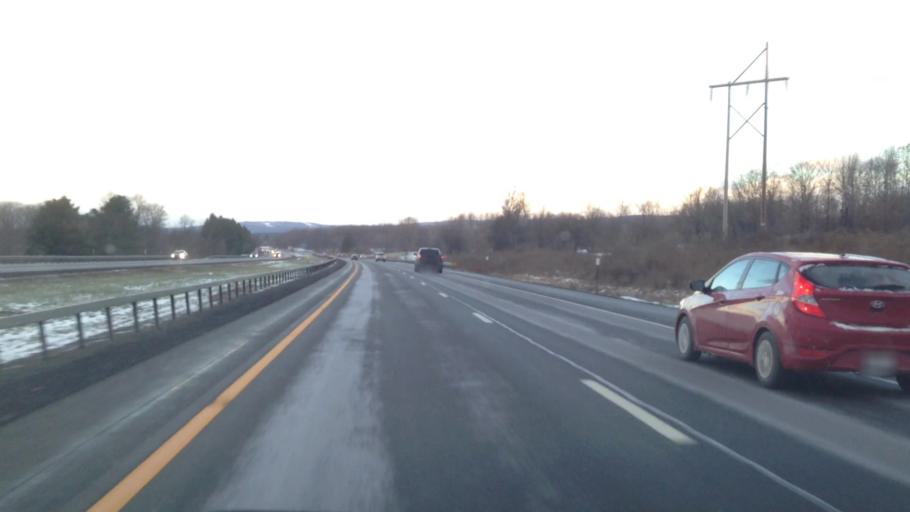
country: US
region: New York
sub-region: Herkimer County
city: Frankfort
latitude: 43.0502
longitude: -75.0610
